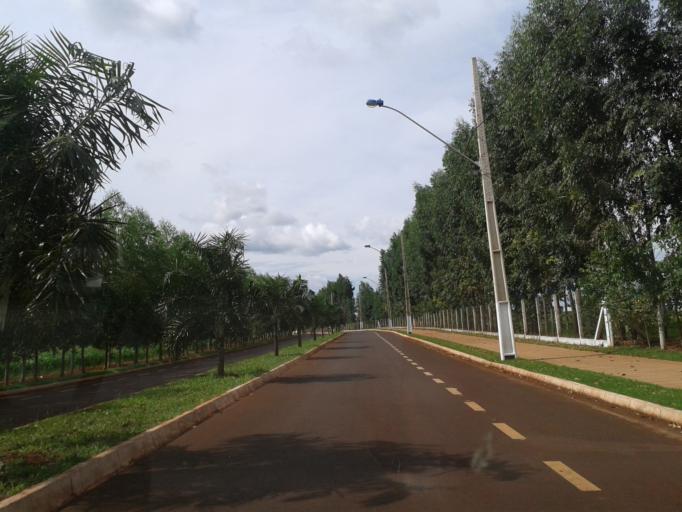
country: BR
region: Minas Gerais
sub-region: Centralina
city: Centralina
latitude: -18.5750
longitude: -49.1962
